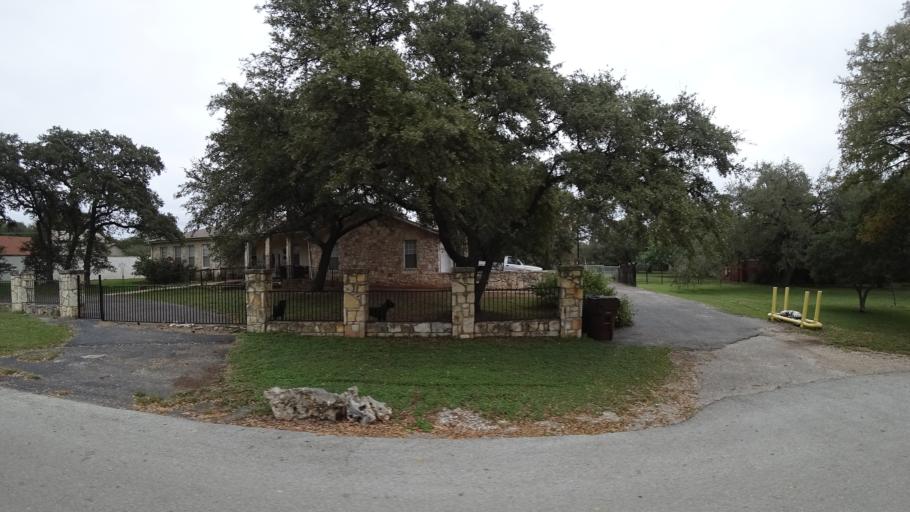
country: US
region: Texas
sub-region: Williamson County
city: Anderson Mill
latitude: 30.4514
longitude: -97.8218
